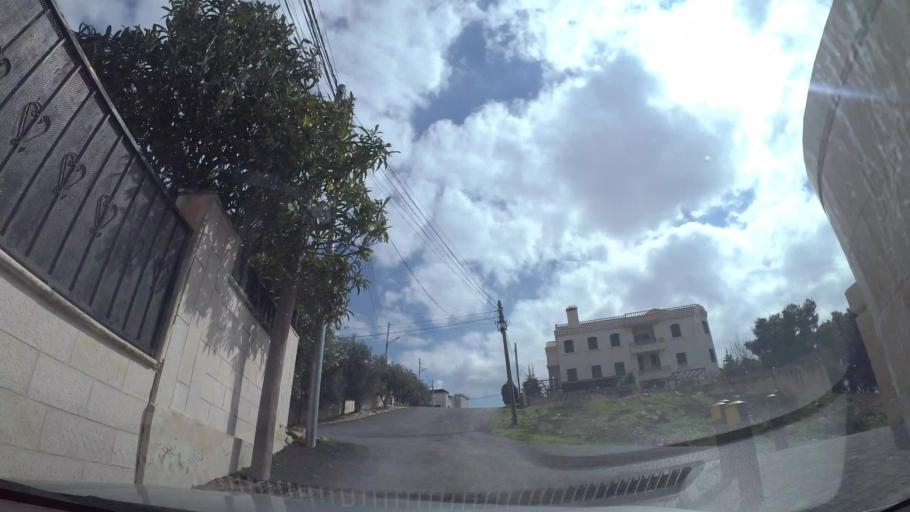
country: JO
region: Amman
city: Al Jubayhah
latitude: 32.0343
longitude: 35.8171
